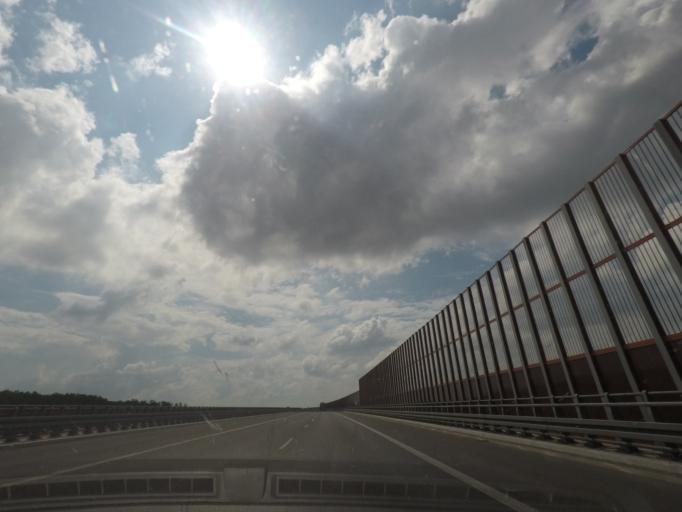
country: PL
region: Lodz Voivodeship
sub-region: Powiat kutnowski
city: Krzyzanow
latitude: 52.1401
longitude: 19.4834
